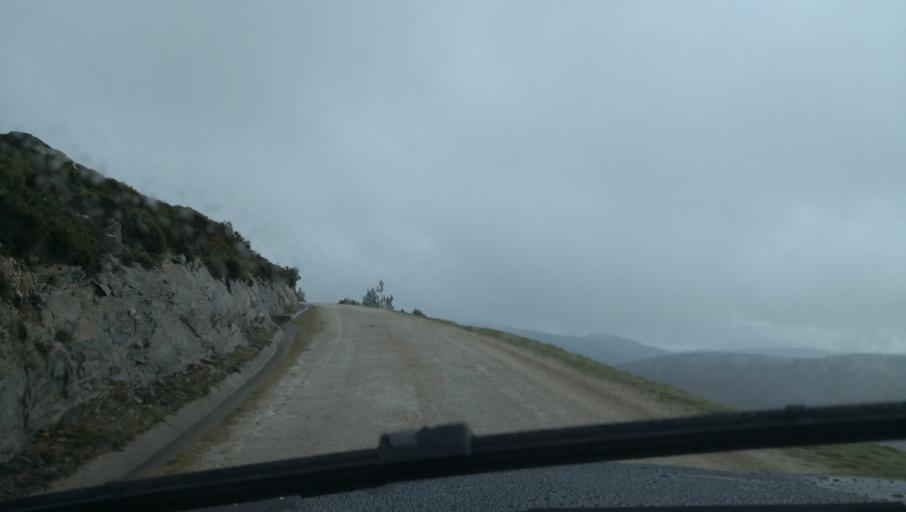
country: PT
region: Vila Real
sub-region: Vila Real
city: Vila Real
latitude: 41.3210
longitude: -7.8643
